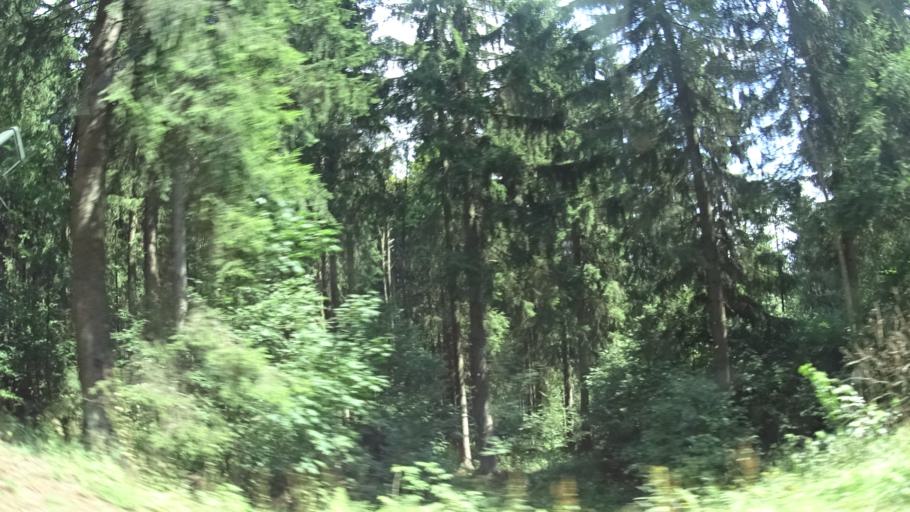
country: DE
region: Thuringia
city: Neustadt am Rennsteig
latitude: 50.5629
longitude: 10.9375
